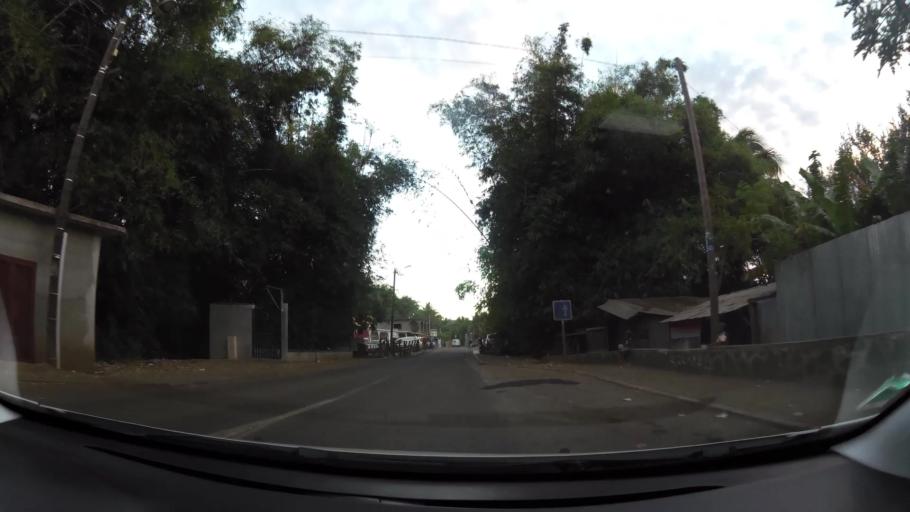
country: YT
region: Koungou
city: Koungou
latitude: -12.7330
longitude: 45.1614
